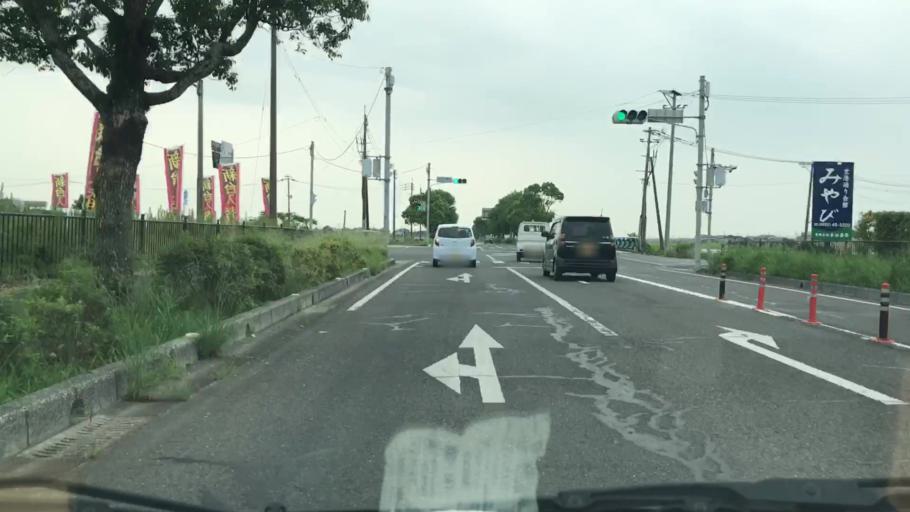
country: JP
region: Saga Prefecture
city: Saga-shi
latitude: 33.2142
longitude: 130.3049
